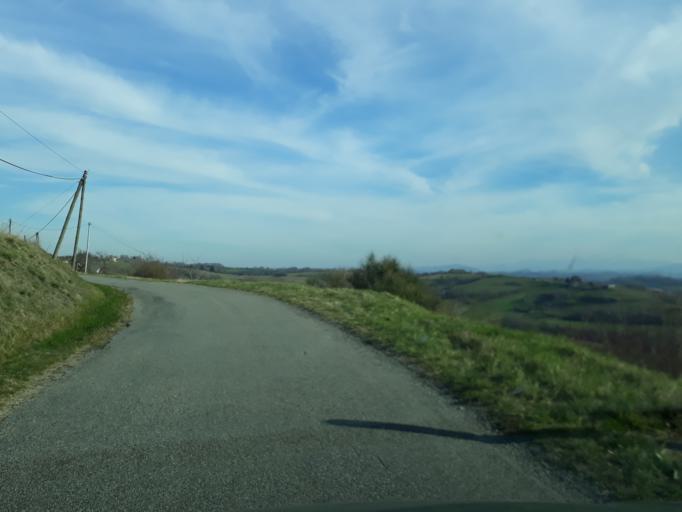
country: FR
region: Midi-Pyrenees
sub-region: Departement de la Haute-Garonne
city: Montesquieu-Volvestre
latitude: 43.1808
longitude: 1.3009
